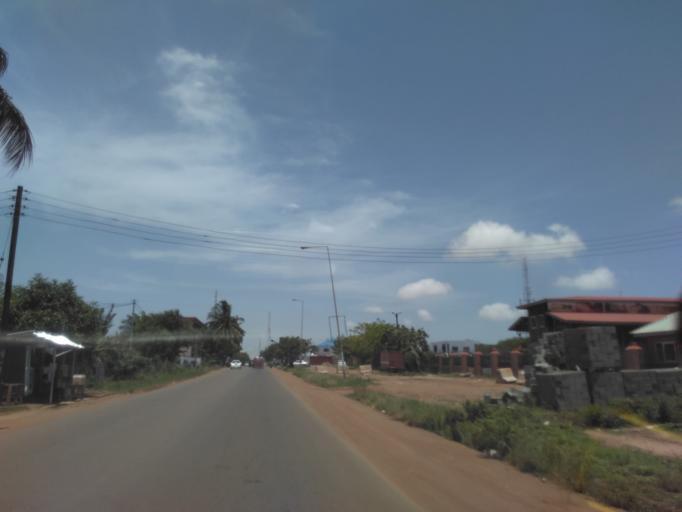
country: GH
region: Greater Accra
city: Tema
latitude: 5.6810
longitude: -0.0182
